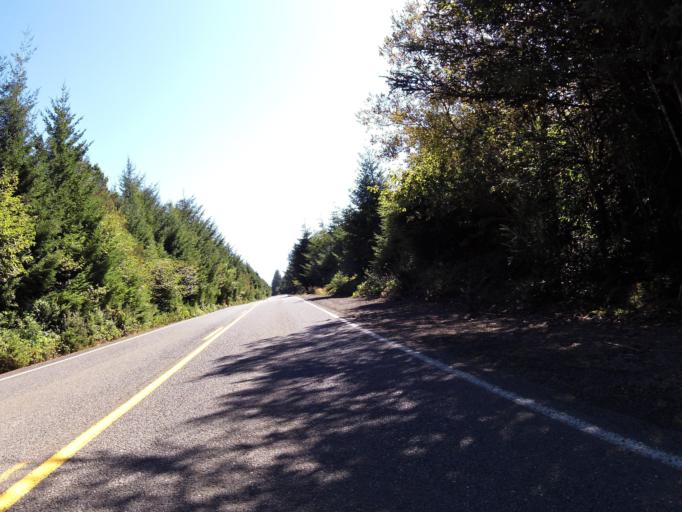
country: US
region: Oregon
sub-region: Coos County
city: Barview
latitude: 43.2658
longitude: -124.3449
